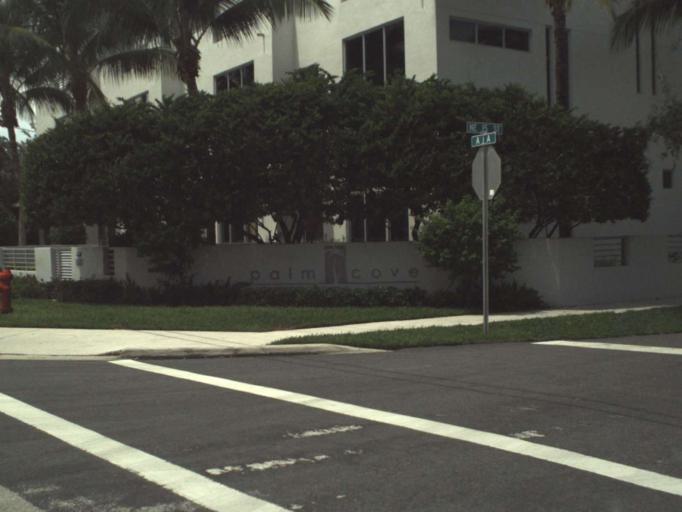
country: US
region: Florida
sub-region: Broward County
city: Lighthouse Point
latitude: 26.2513
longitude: -80.0865
